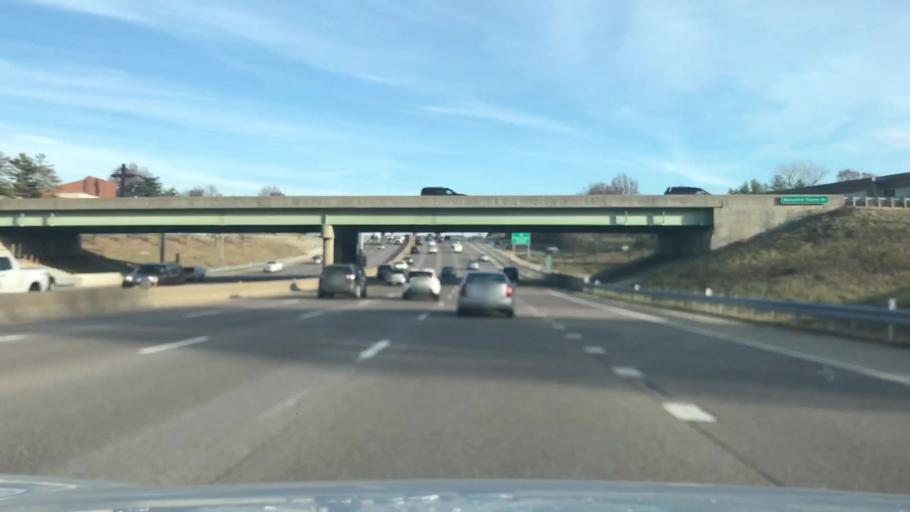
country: US
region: Missouri
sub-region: Saint Louis County
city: Town and Country
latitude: 38.6410
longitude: -90.4960
